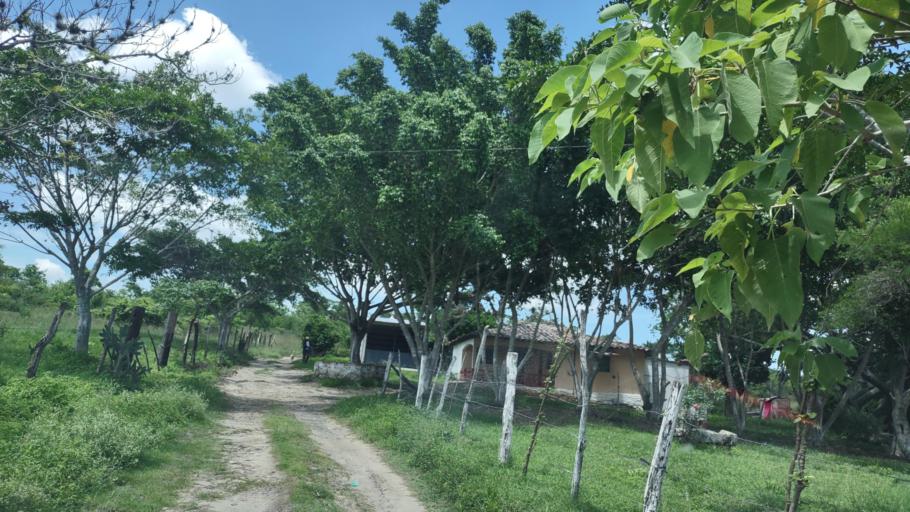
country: MX
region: Veracruz
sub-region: Emiliano Zapata
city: Dos Rios
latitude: 19.5006
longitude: -96.8101
